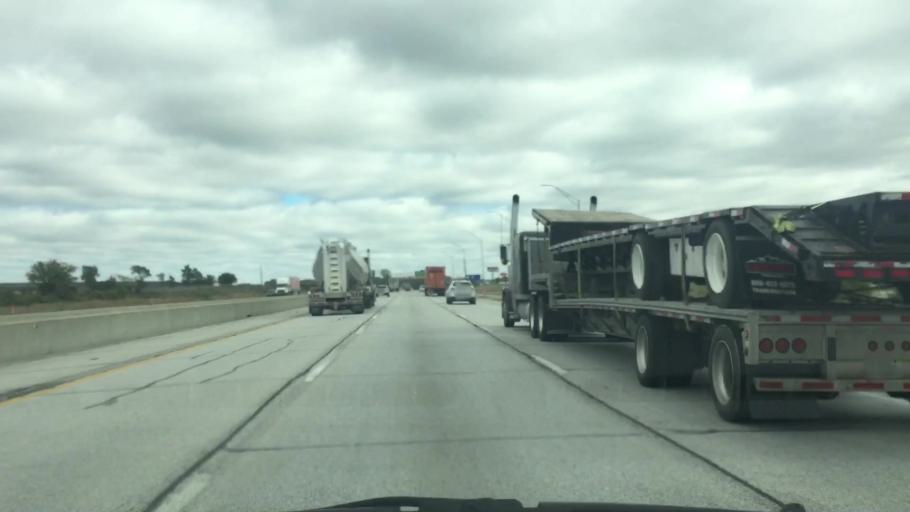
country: US
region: Iowa
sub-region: Polk County
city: Altoona
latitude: 41.6607
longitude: -93.5169
